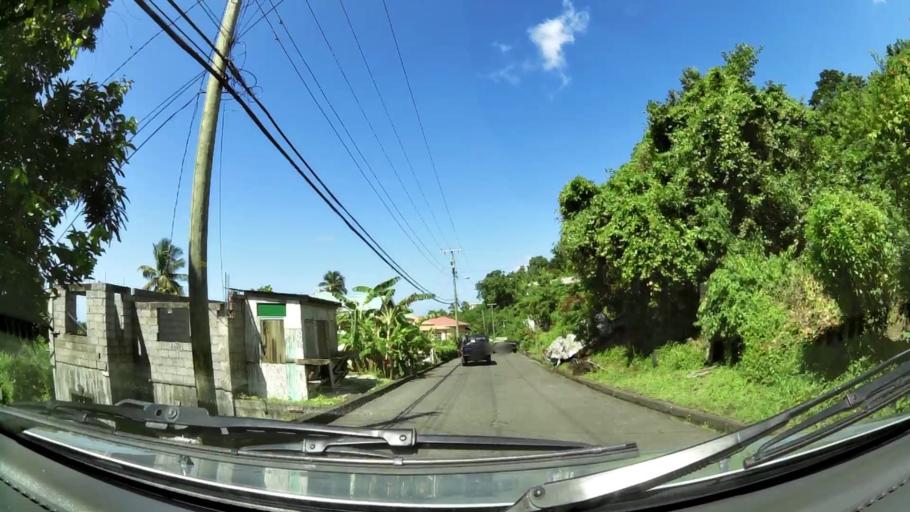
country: GD
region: Saint John
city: Gouyave
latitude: 12.1275
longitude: -61.7472
